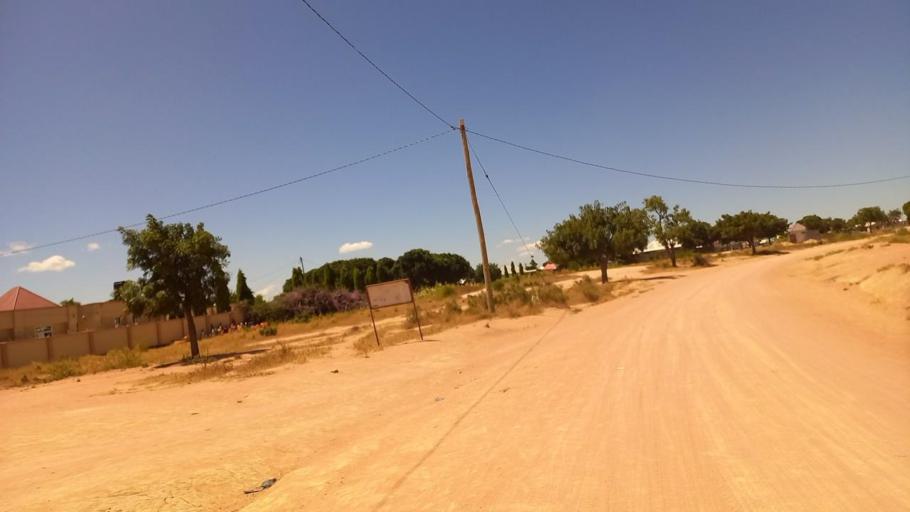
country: TZ
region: Dodoma
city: Dodoma
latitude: -6.1296
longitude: 35.7301
